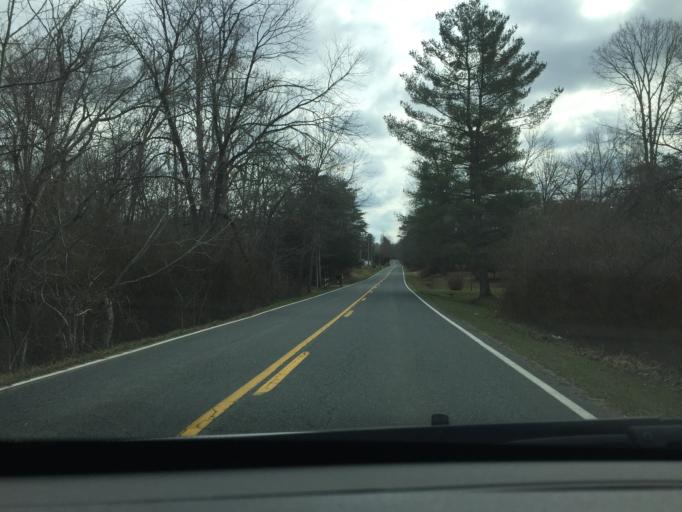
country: US
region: Virginia
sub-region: Campbell County
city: Rustburg
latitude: 37.3280
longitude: -79.1563
